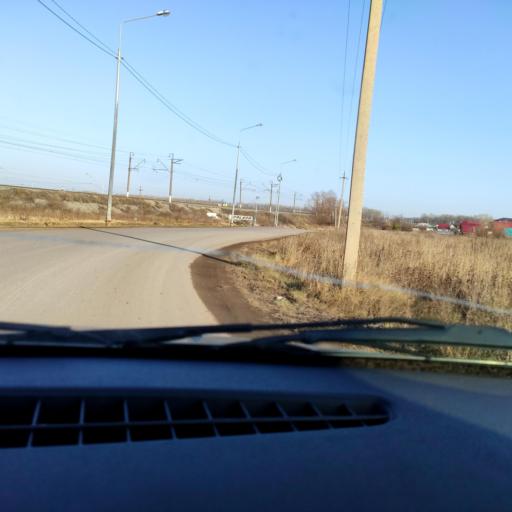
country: RU
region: Bashkortostan
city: Kabakovo
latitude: 54.6391
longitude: 56.0771
